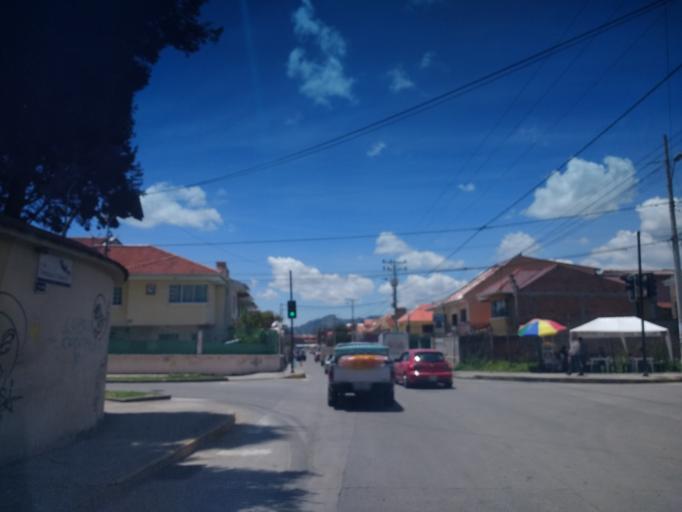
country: EC
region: Azuay
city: Cuenca
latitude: -2.8980
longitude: -79.0340
